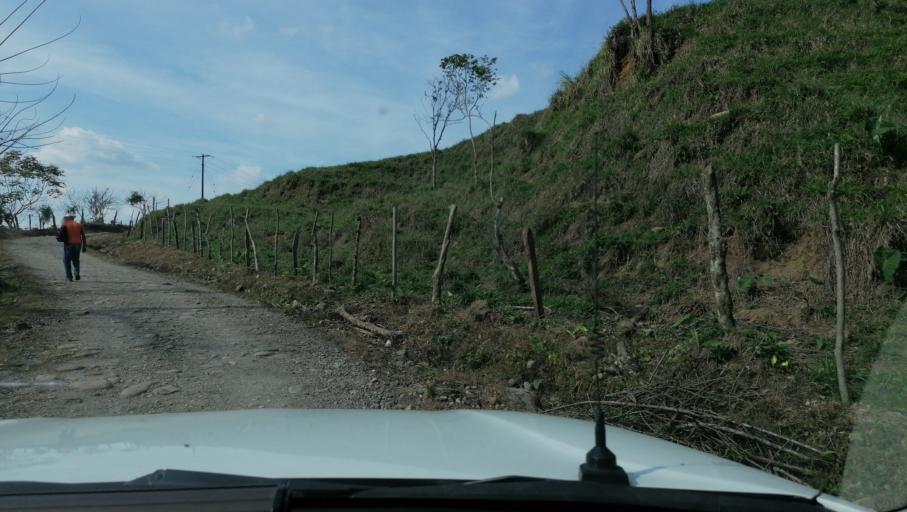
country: MX
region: Chiapas
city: Ostuacan
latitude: 17.4592
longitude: -93.2408
